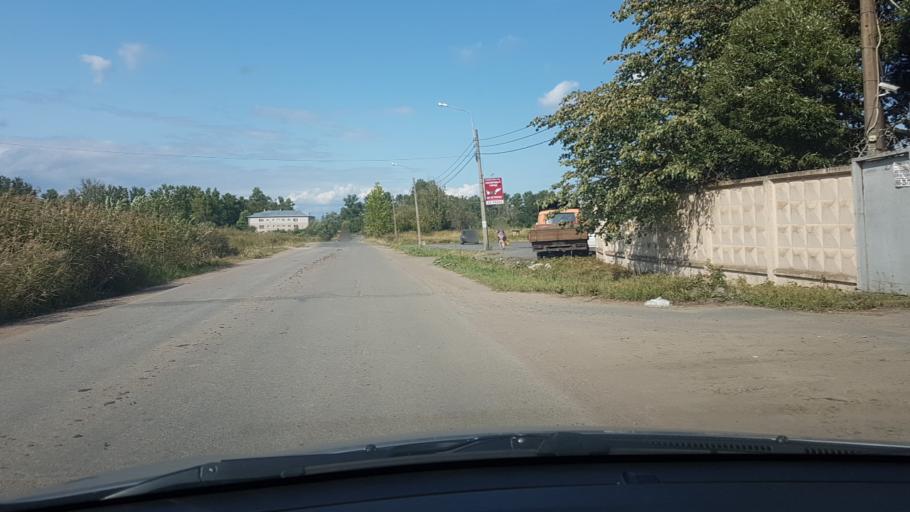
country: RU
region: St.-Petersburg
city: Sosnovaya Polyana
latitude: 59.8439
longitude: 30.1195
